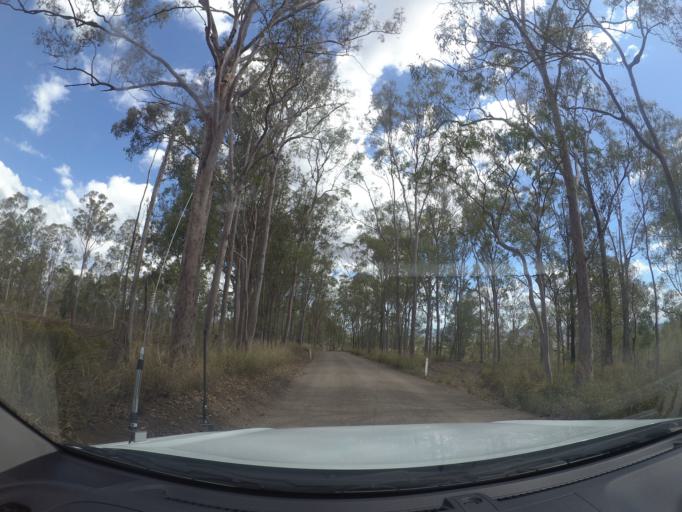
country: AU
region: Queensland
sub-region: Logan
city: Cedar Vale
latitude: -27.9000
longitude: 152.9871
